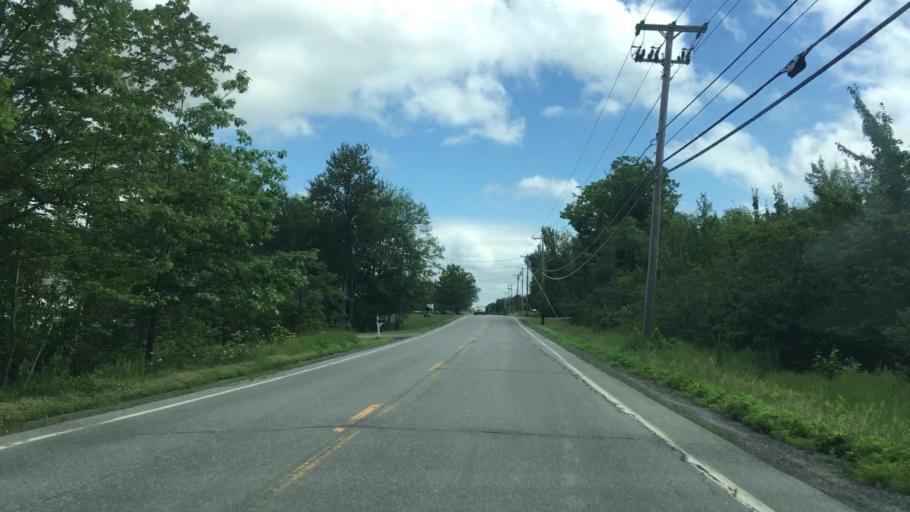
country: US
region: Maine
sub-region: Penobscot County
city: Hermon
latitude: 44.8074
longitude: -68.9334
